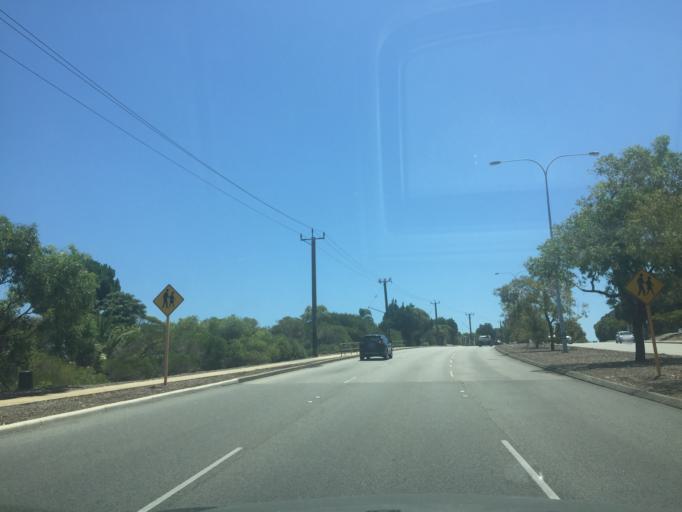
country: AU
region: Western Australia
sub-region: Melville
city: Kardinya
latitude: -32.0687
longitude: 115.8129
